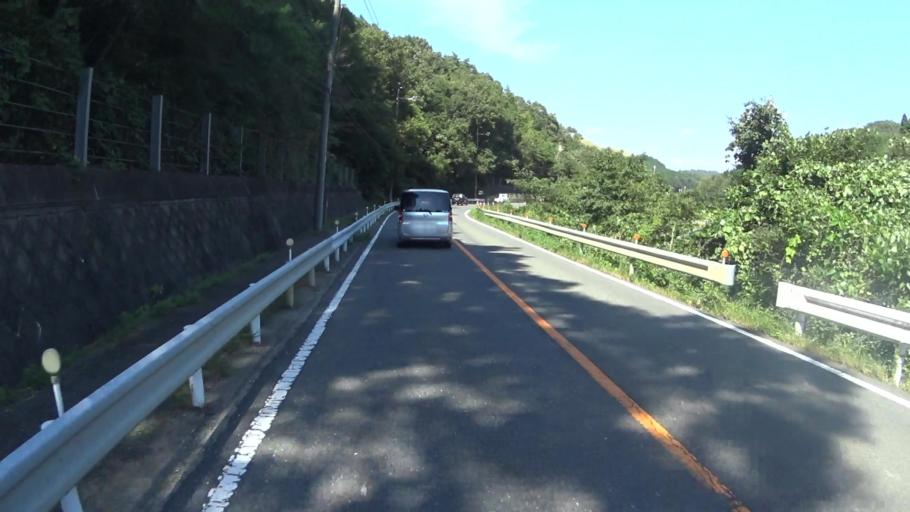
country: JP
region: Kyoto
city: Kameoka
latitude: 34.9694
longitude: 135.5164
